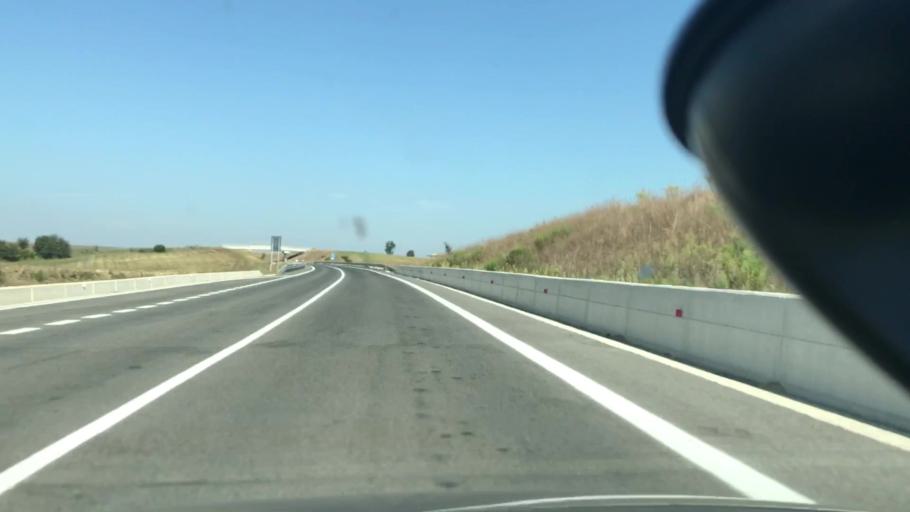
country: IT
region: Basilicate
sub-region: Provincia di Potenza
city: Palazzo San Gervasio
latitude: 40.9651
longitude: 16.0093
